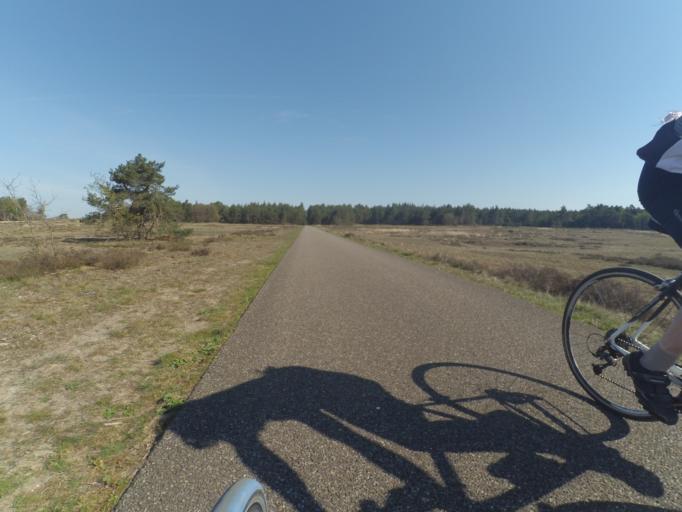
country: NL
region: Gelderland
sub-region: Gemeente Ede
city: Harskamp
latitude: 52.1756
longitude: 5.8156
